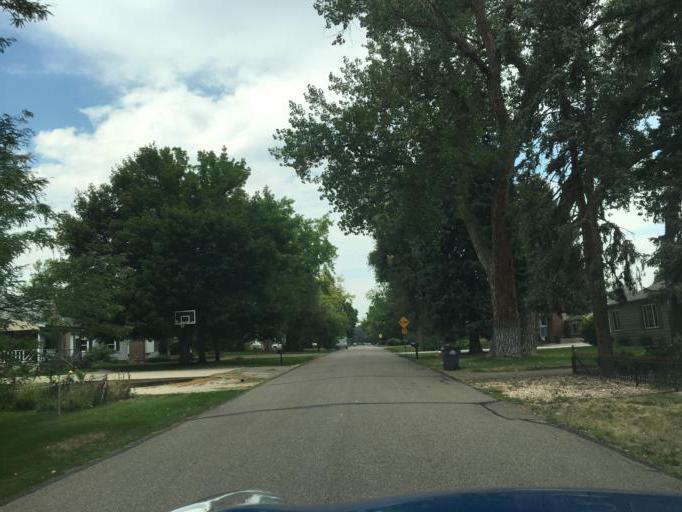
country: US
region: Colorado
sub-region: Jefferson County
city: Wheat Ridge
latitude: 39.7491
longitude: -105.0950
